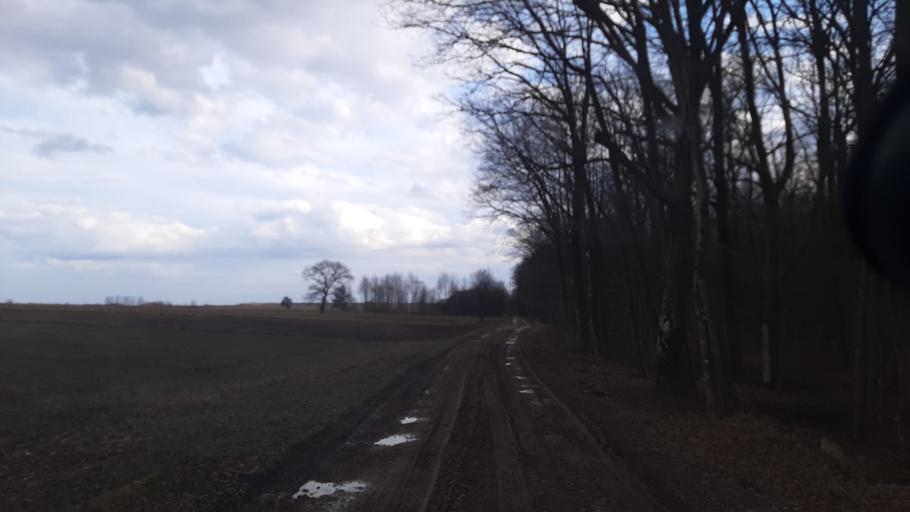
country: PL
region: Lublin Voivodeship
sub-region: Powiat lubelski
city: Jastkow
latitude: 51.3729
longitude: 22.4157
